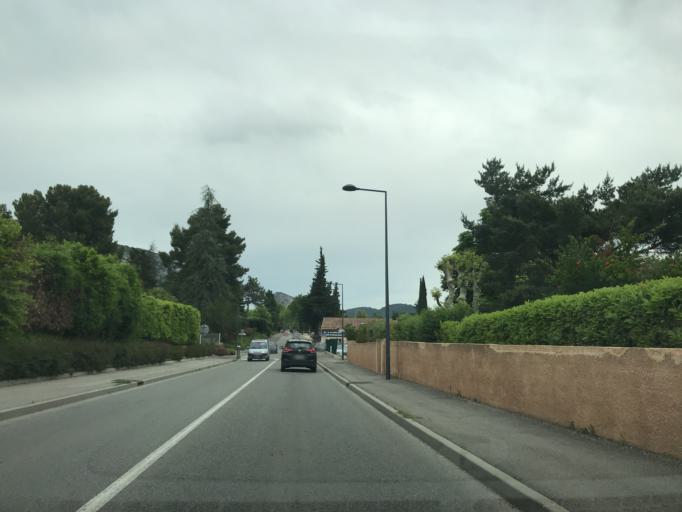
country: FR
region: Provence-Alpes-Cote d'Azur
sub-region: Departement des Alpes-de-Haute-Provence
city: Volx
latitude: 43.8697
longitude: 5.8432
